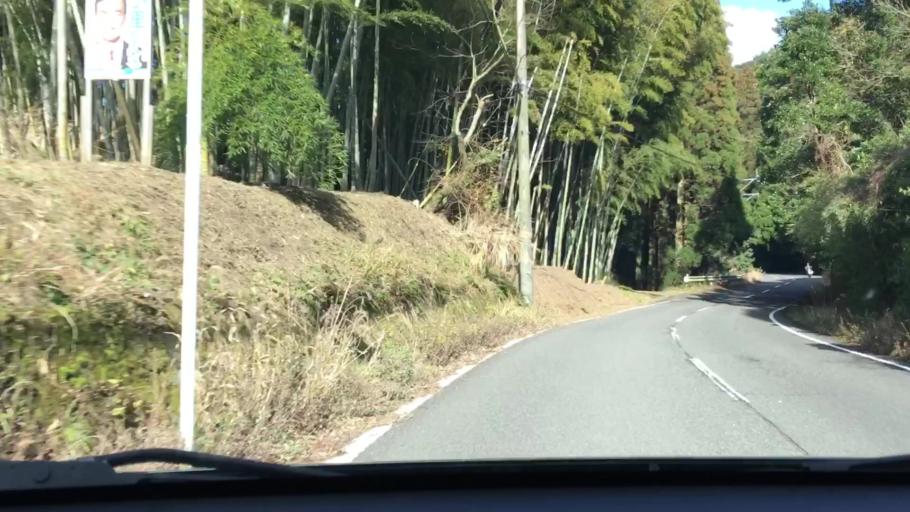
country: JP
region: Kagoshima
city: Ijuin
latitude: 31.7285
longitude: 130.4188
